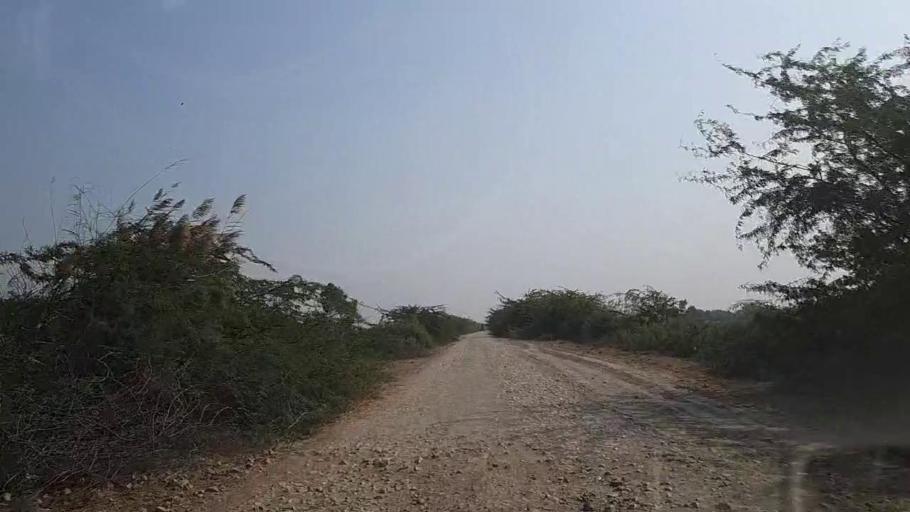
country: PK
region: Sindh
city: Keti Bandar
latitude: 24.2499
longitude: 67.6305
